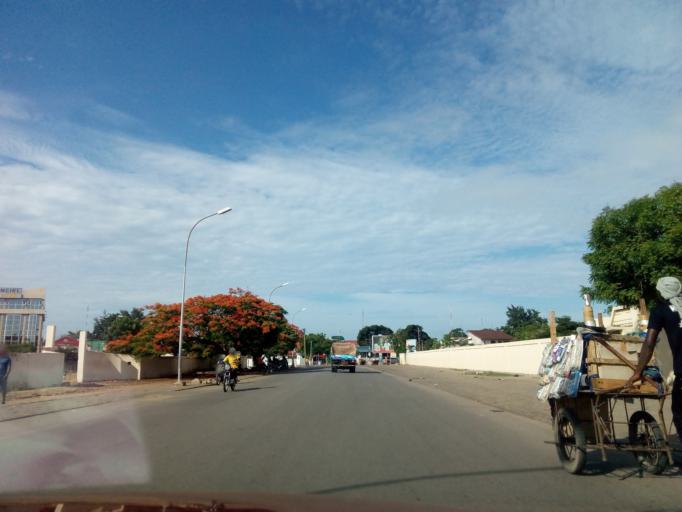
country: BJ
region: Littoral
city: Cotonou
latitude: 6.3571
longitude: 2.4178
